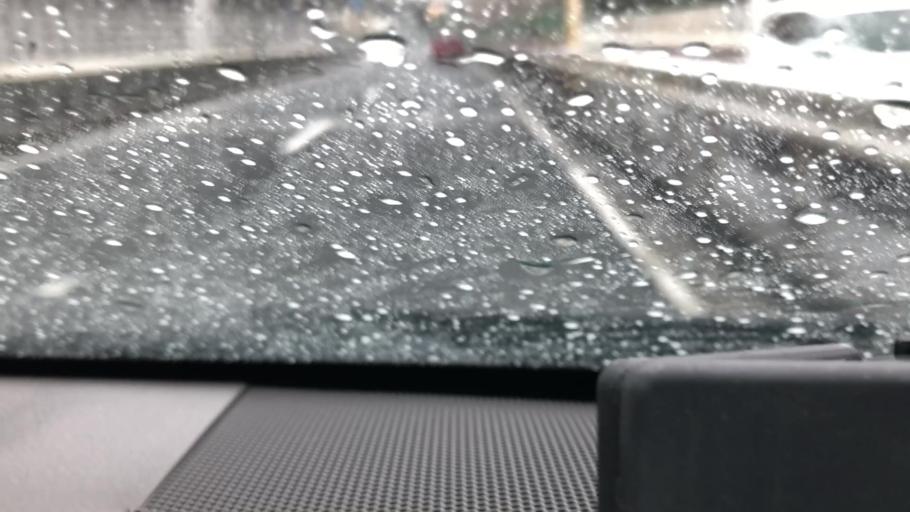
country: JP
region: Kanagawa
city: Yokohama
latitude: 35.4392
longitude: 139.6002
